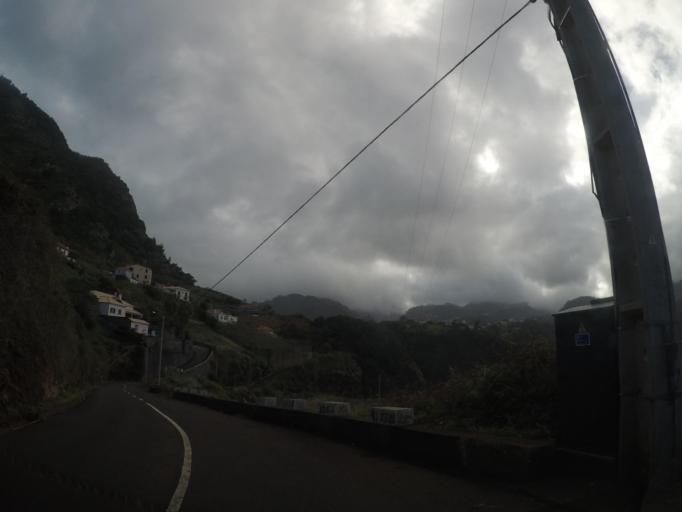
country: PT
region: Madeira
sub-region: Santana
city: Santana
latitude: 32.7877
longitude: -16.8485
